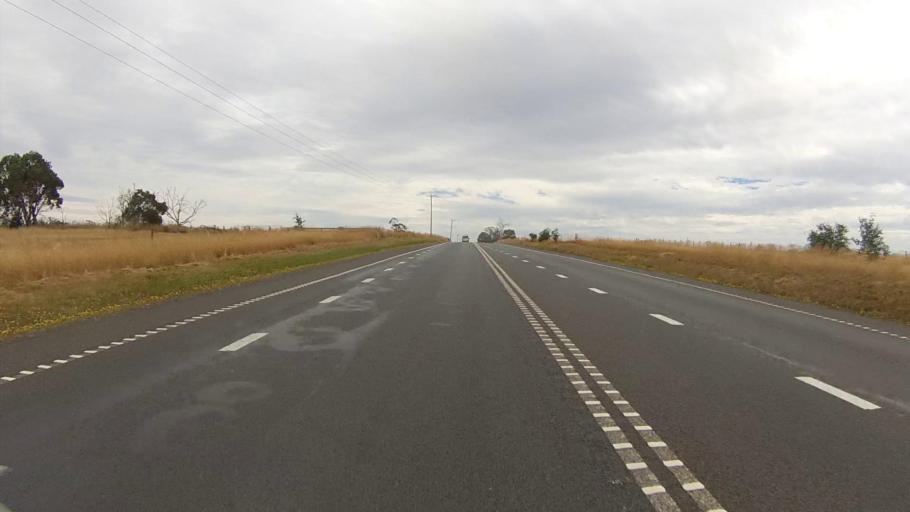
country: AU
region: Tasmania
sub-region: Northern Midlands
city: Evandale
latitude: -41.7087
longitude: 147.2998
